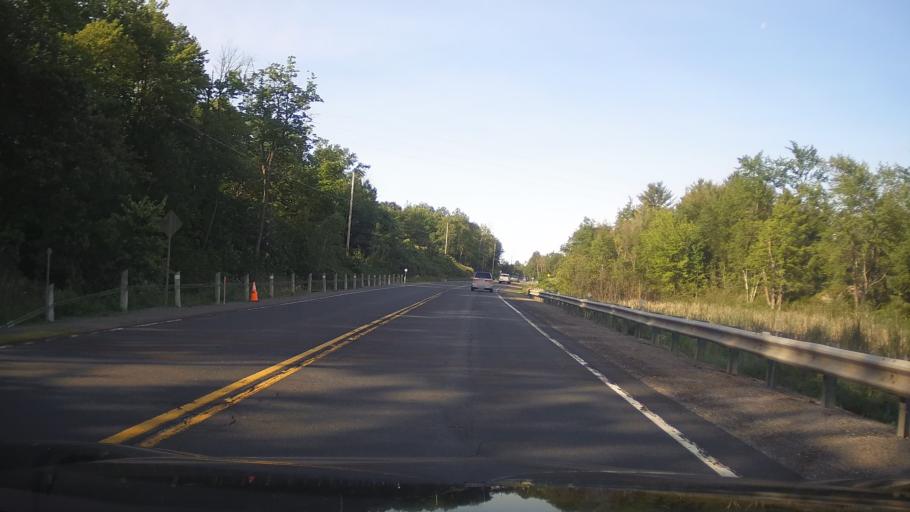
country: CA
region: Ontario
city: Greater Napanee
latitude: 44.6004
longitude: -77.1867
